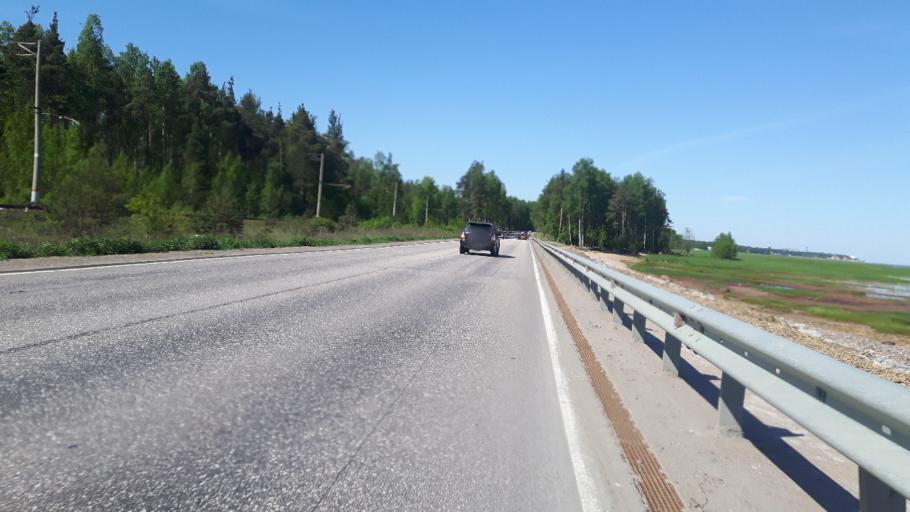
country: RU
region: Leningrad
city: Lebyazh'ye
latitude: 59.9567
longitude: 29.4792
